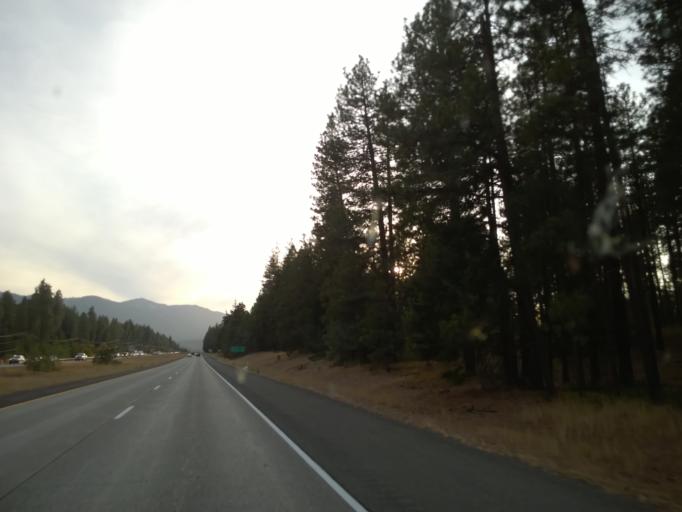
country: US
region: Washington
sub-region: Kittitas County
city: Cle Elum
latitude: 47.1915
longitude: -120.9740
